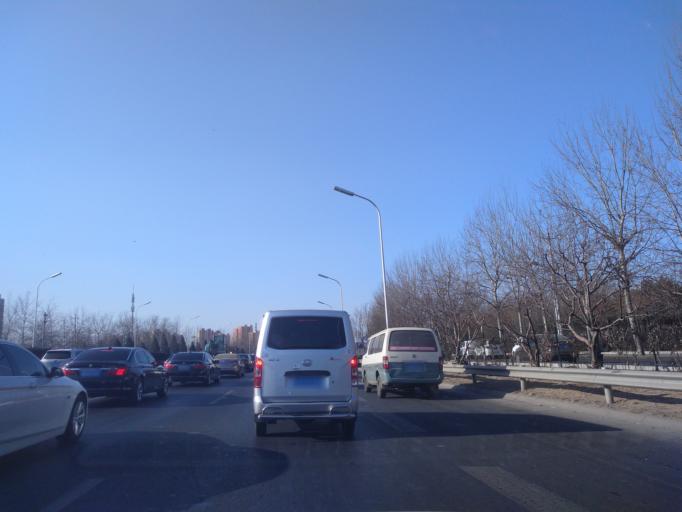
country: CN
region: Beijing
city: Jiugong
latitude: 39.8341
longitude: 116.4613
